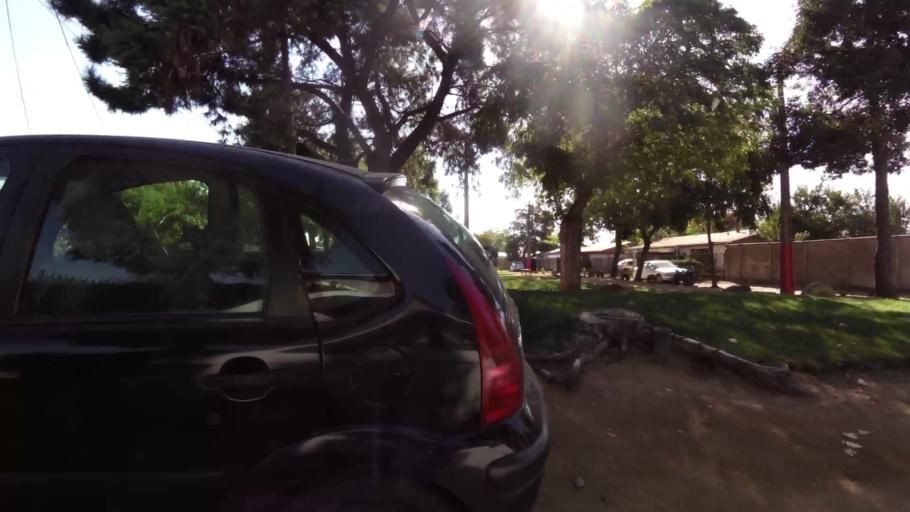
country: CL
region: Maule
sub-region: Provincia de Talca
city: Talca
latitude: -35.4490
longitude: -71.6546
